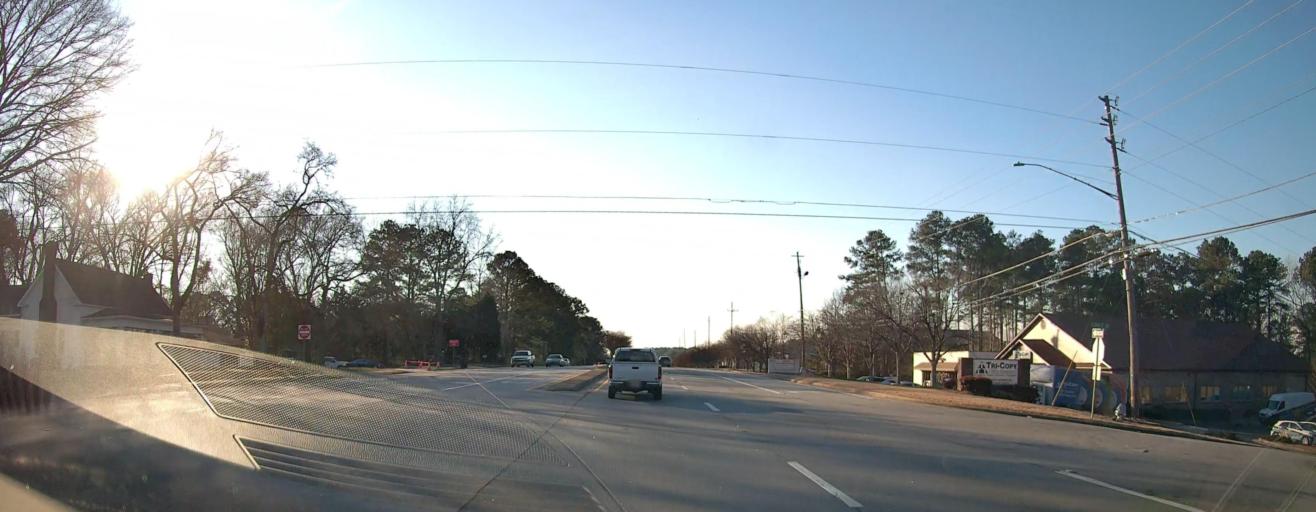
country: US
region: Georgia
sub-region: Fayette County
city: Fayetteville
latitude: 33.4469
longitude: -84.4712
